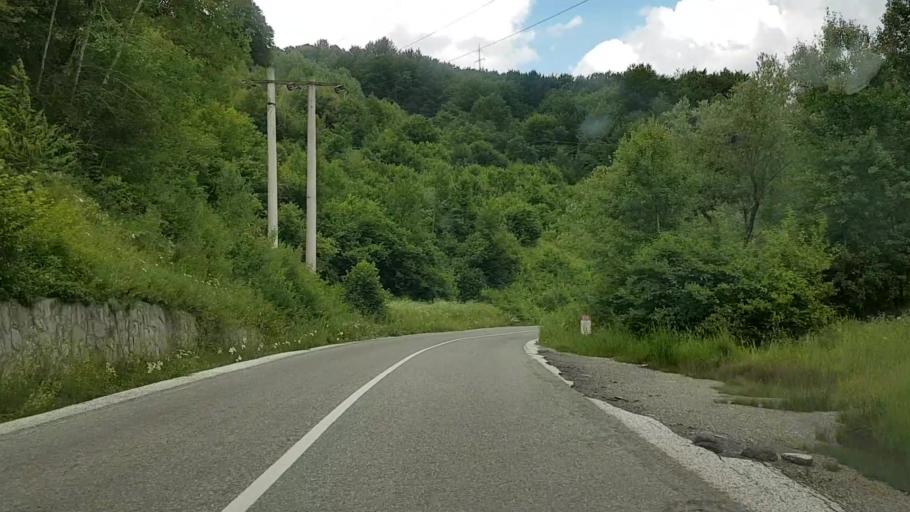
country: RO
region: Neamt
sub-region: Comuna Pangarati
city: Pangarati
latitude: 46.9580
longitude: 26.1239
